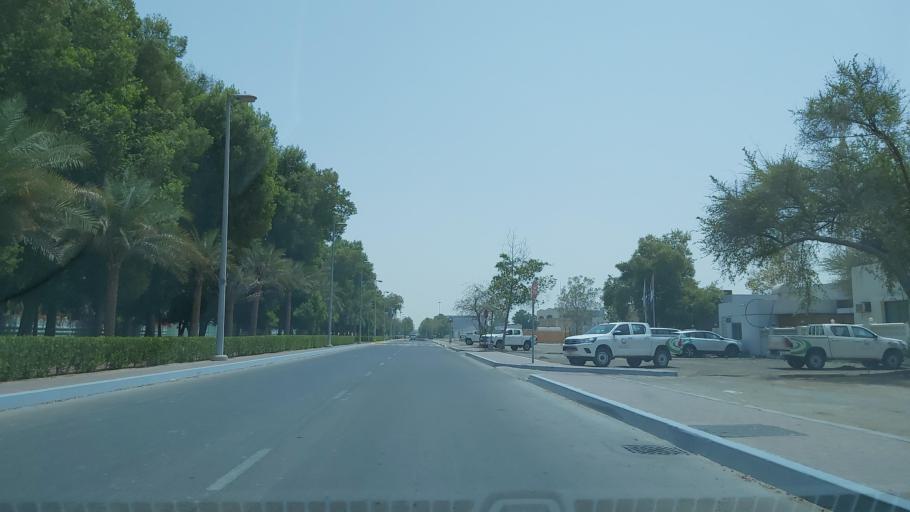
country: AE
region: Abu Dhabi
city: Abu Dhabi
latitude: 24.3792
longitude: 54.5183
